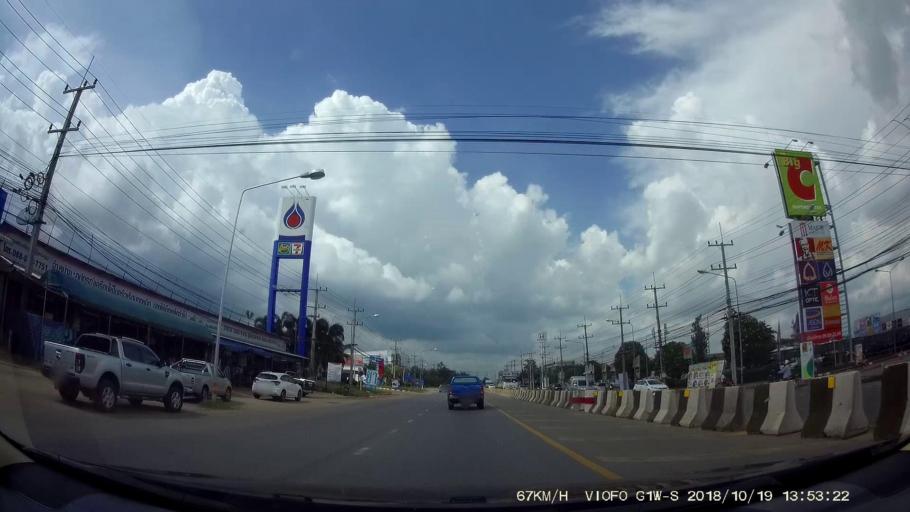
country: TH
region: Chaiyaphum
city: Chaiyaphum
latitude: 15.7770
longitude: 102.0255
